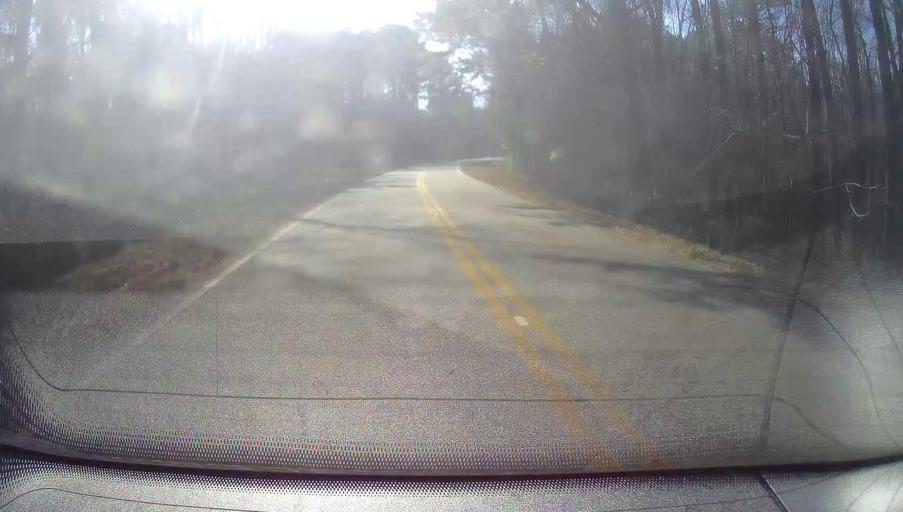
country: US
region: Georgia
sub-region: Monroe County
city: Forsyth
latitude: 33.0593
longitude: -83.8690
